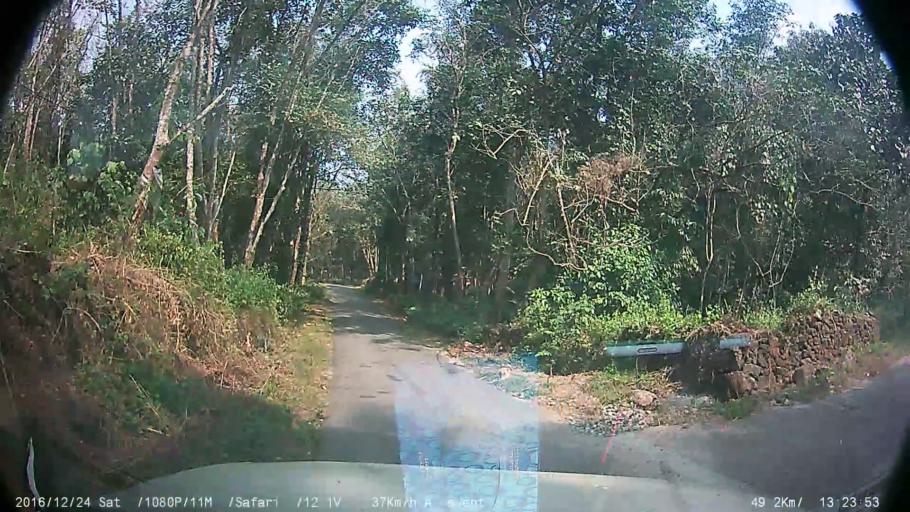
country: IN
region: Kerala
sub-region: Kottayam
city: Palackattumala
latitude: 9.8697
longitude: 76.6736
